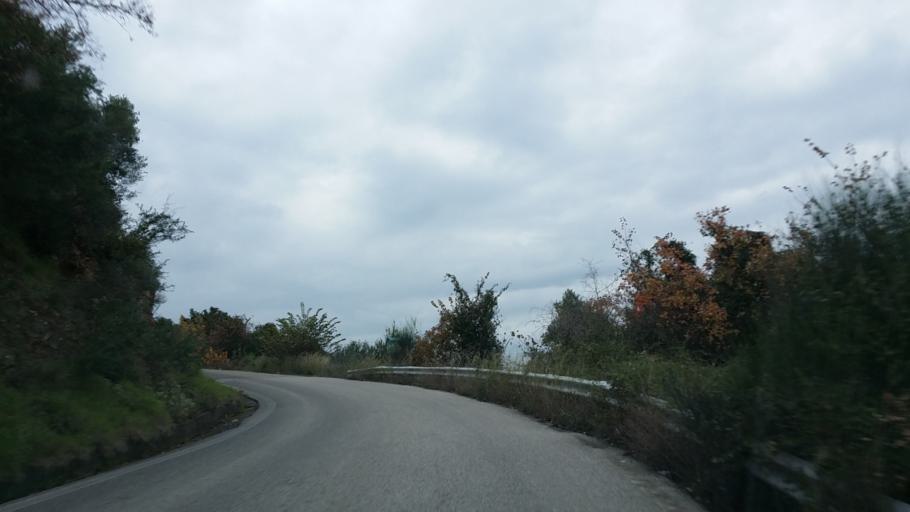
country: GR
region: West Greece
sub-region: Nomos Aitolias kai Akarnanias
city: Fitiai
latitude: 38.7200
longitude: 21.1871
